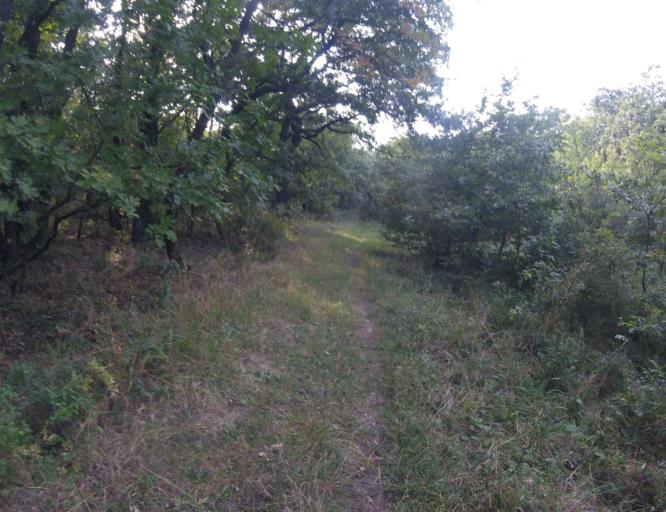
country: HU
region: Pest
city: Nagykovacsi
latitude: 47.6777
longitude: 19.0165
